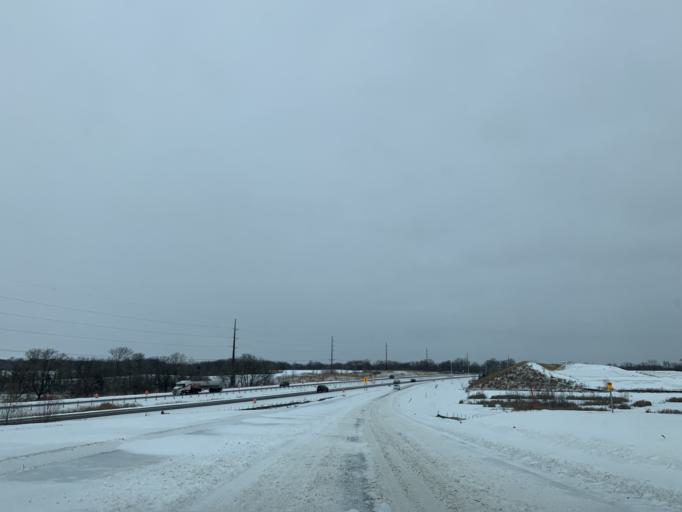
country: US
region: Minnesota
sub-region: Carver County
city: Chaska
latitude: 44.7921
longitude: -93.6310
